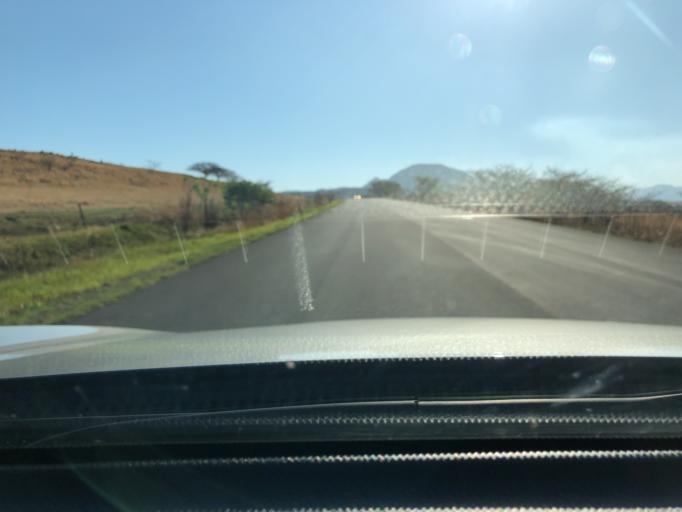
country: ZA
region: KwaZulu-Natal
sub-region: uThukela District Municipality
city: Ladysmith
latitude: -28.4018
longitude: 29.9379
